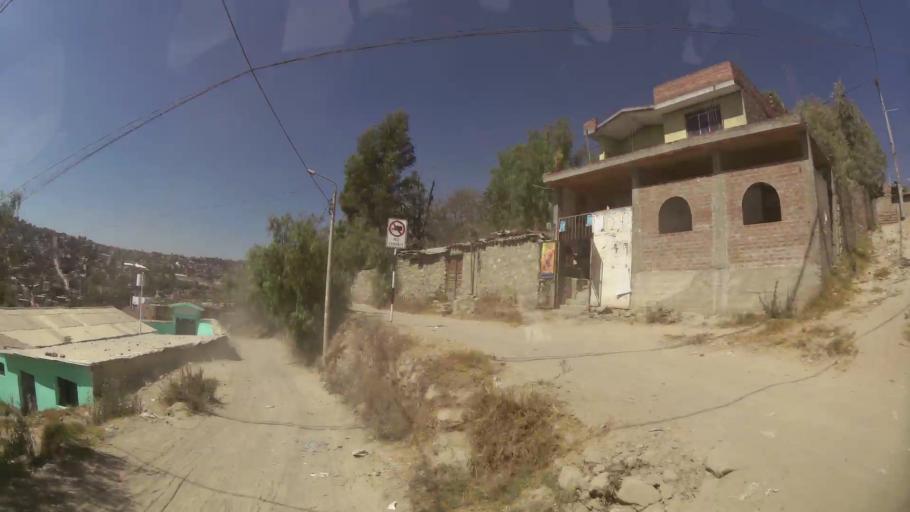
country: PE
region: Ayacucho
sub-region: Provincia de Huamanga
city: Carmen Alto
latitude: -13.1727
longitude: -74.2300
